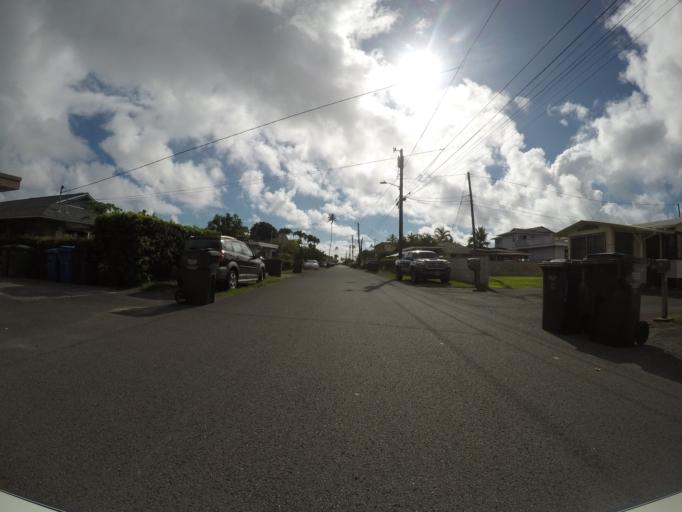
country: US
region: Hawaii
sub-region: Honolulu County
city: Kailua
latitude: 21.4003
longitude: -157.7472
